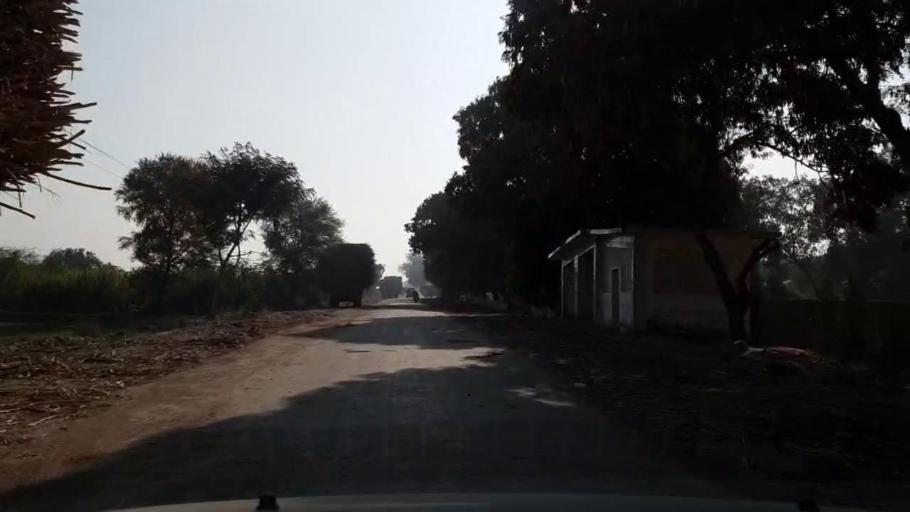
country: PK
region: Sindh
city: Matiari
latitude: 25.5781
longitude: 68.5012
